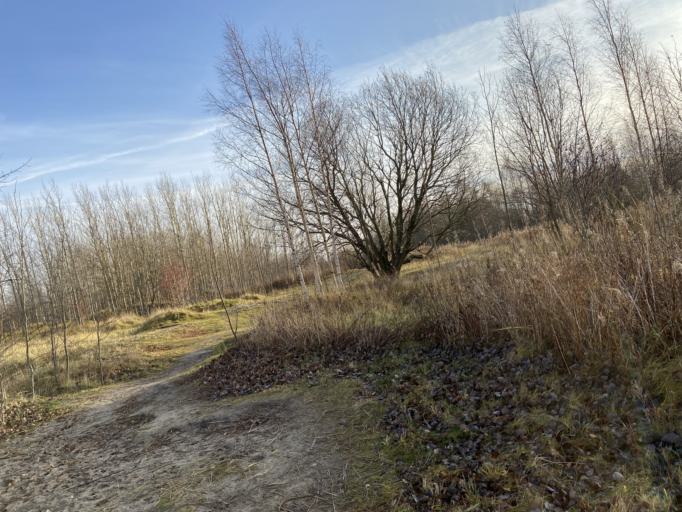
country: EE
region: Harju
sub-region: Tallinna linn
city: Tallinn
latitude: 59.4758
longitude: 24.7181
